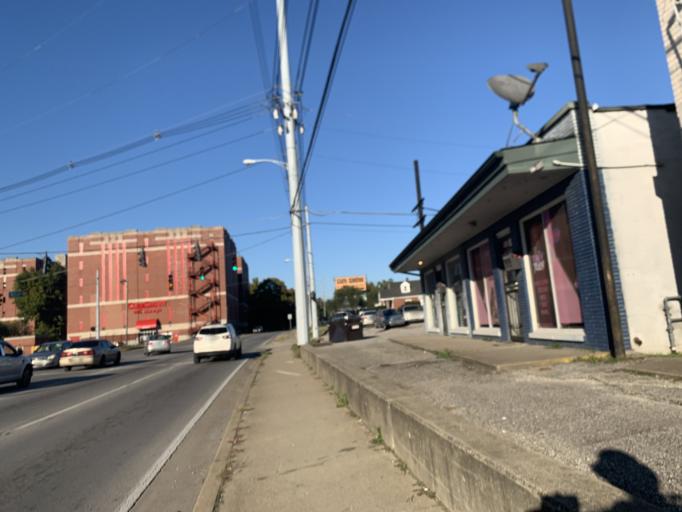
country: US
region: Kentucky
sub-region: Jefferson County
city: Shively
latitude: 38.2126
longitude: -85.7849
